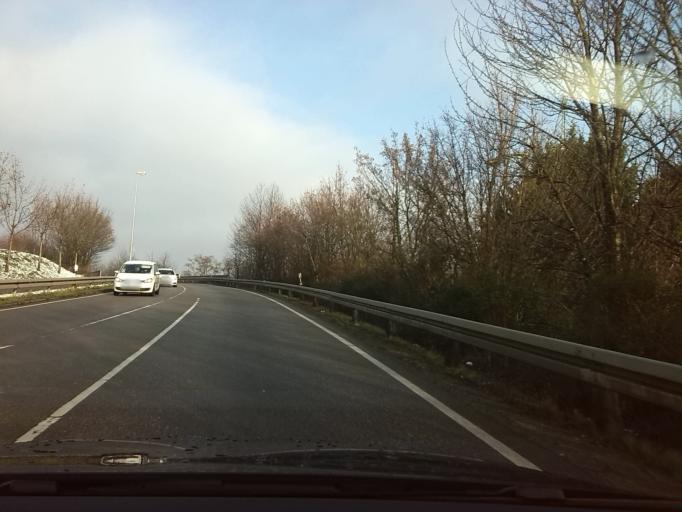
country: DE
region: Baden-Wuerttemberg
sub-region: Regierungsbezirk Stuttgart
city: Fellbach
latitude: 48.8233
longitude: 9.2871
